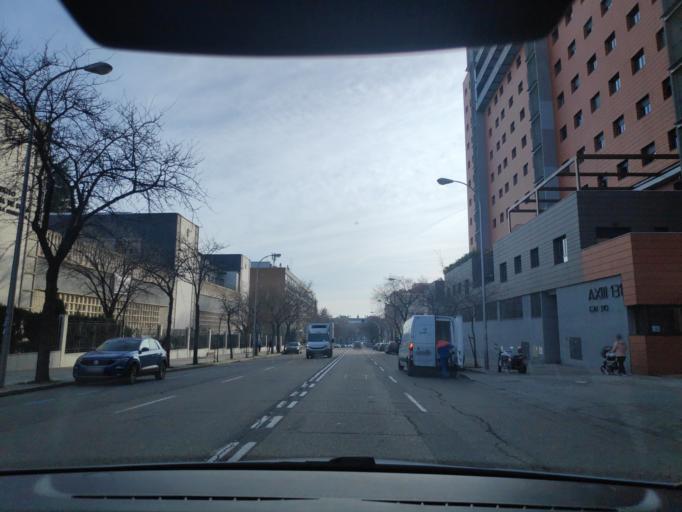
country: ES
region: Madrid
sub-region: Provincia de Madrid
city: Chamartin
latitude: 40.4603
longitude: -3.6731
